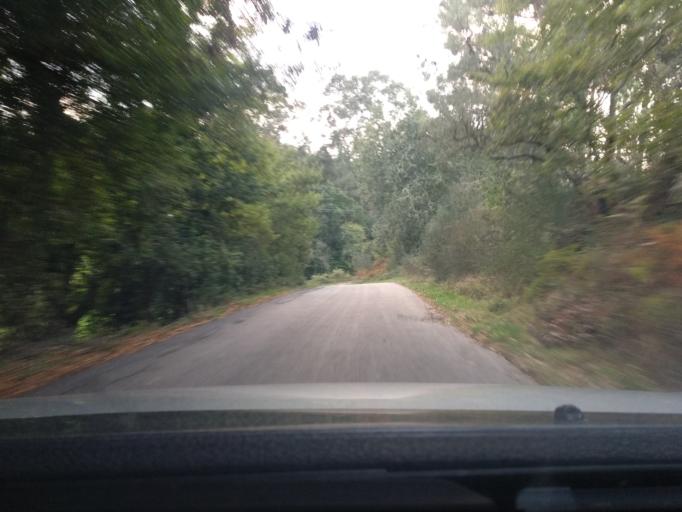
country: ES
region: Galicia
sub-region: Provincia de Pontevedra
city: Moana
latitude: 42.3048
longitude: -8.6958
